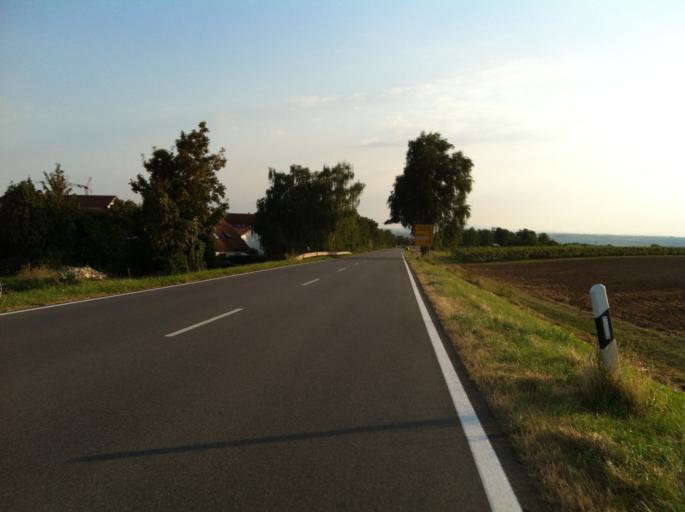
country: DE
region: Rheinland-Pfalz
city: Essenheim
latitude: 49.9310
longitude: 8.1511
